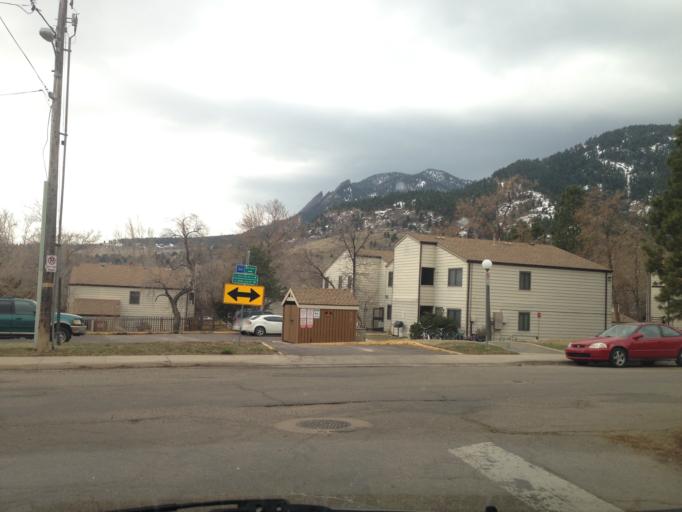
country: US
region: Colorado
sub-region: Boulder County
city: Boulder
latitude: 40.0168
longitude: -105.2915
